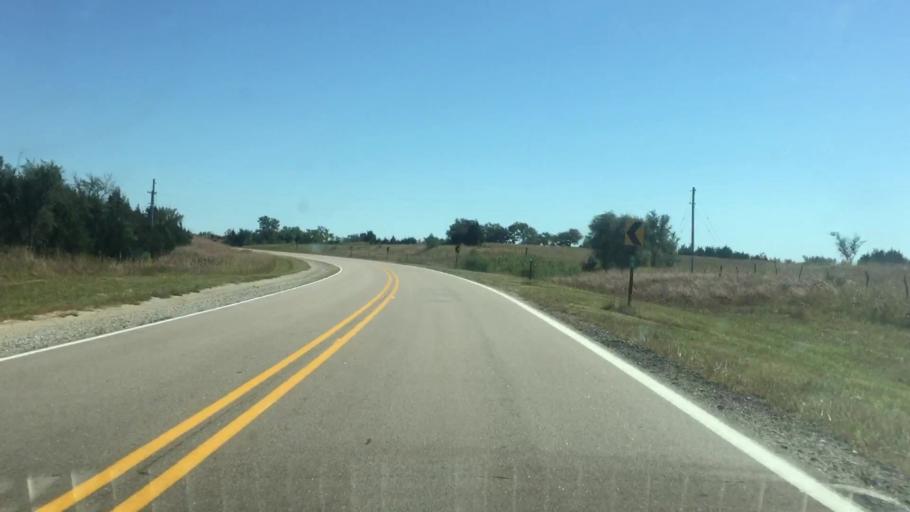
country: US
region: Nebraska
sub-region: Jefferson County
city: Fairbury
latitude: 40.0420
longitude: -97.0185
